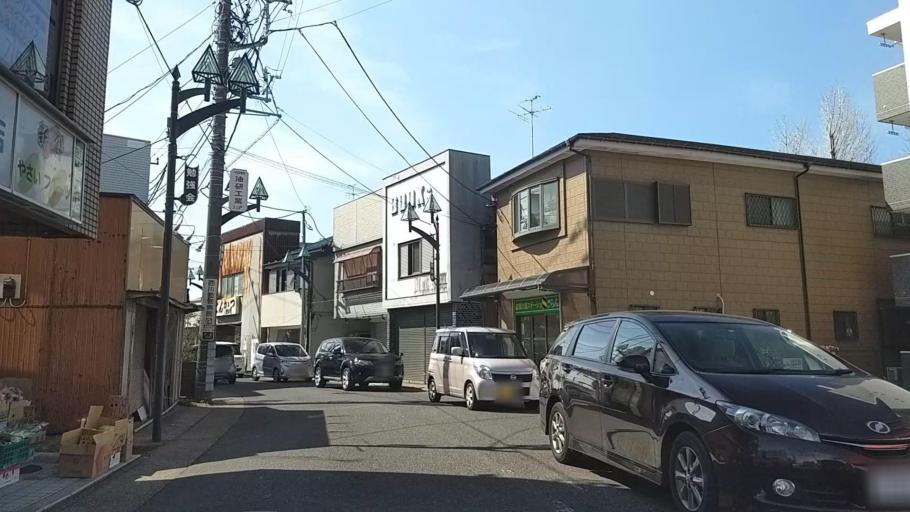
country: JP
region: Kanagawa
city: Minami-rinkan
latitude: 35.4137
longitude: 139.4654
